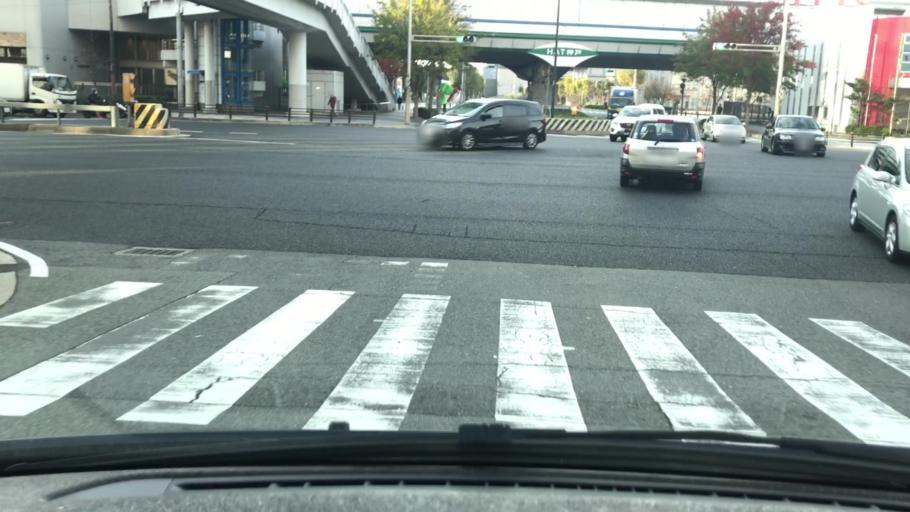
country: JP
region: Hyogo
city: Kobe
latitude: 34.7028
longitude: 135.2175
